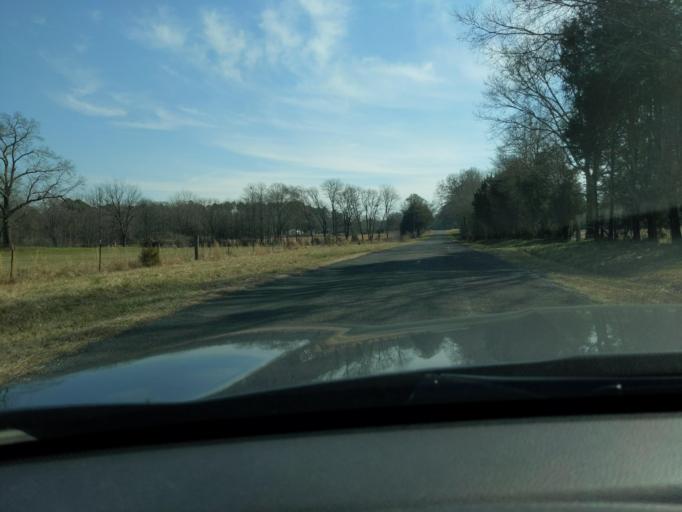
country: US
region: South Carolina
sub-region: Abbeville County
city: Calhoun Falls
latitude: 34.0944
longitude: -82.5648
